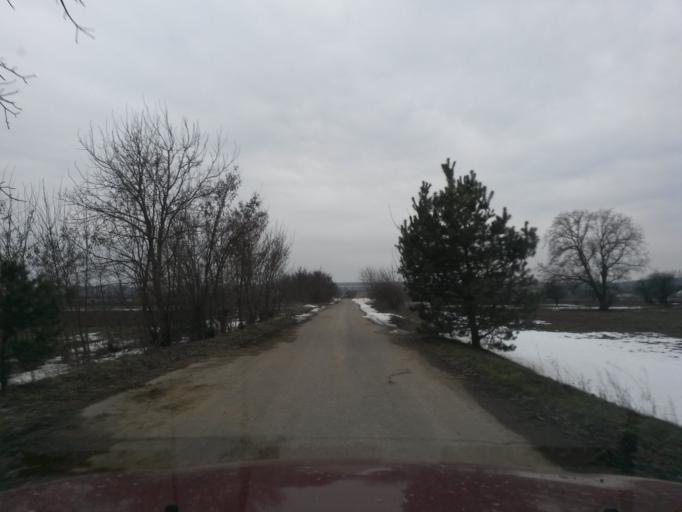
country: SK
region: Kosicky
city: Michalovce
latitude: 48.7284
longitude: 21.8778
